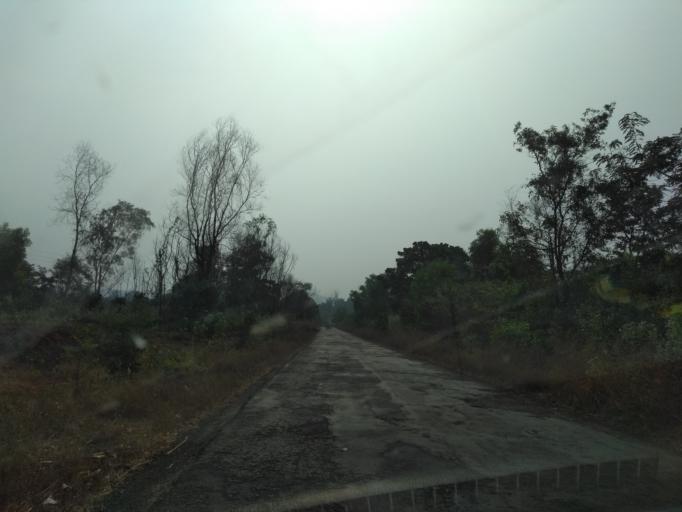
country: IN
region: Maharashtra
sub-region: Sindhudurg
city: Savantvadi
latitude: 15.8092
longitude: 73.9075
